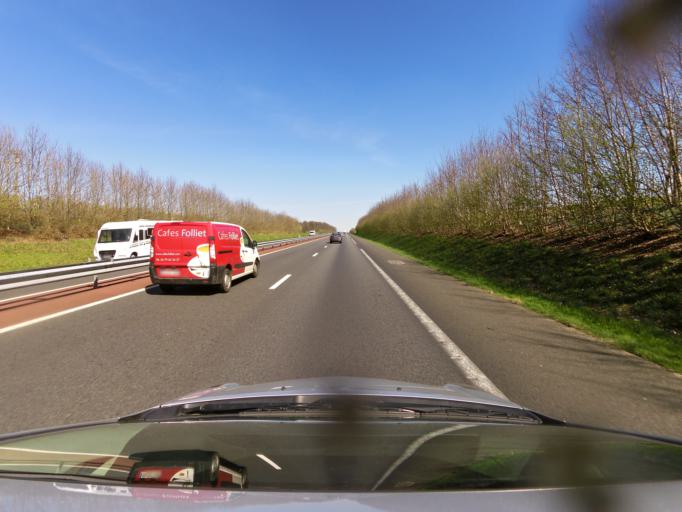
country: FR
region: Lower Normandy
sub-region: Departement de la Manche
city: Saint-Senier-sous-Avranches
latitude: 48.7594
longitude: -1.2784
